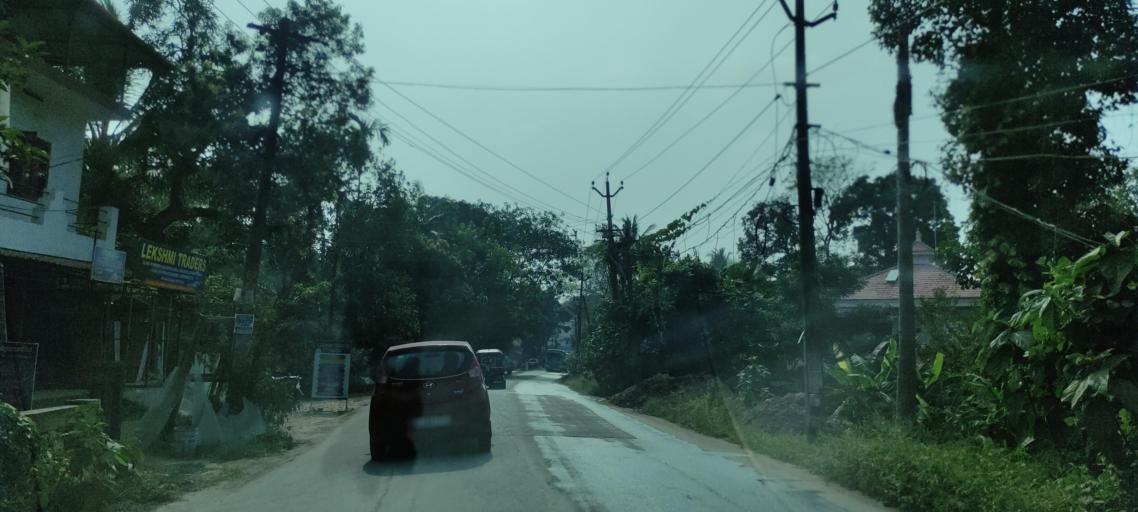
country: IN
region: Kerala
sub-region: Pattanamtitta
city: Tiruvalla
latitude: 9.3782
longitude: 76.5594
